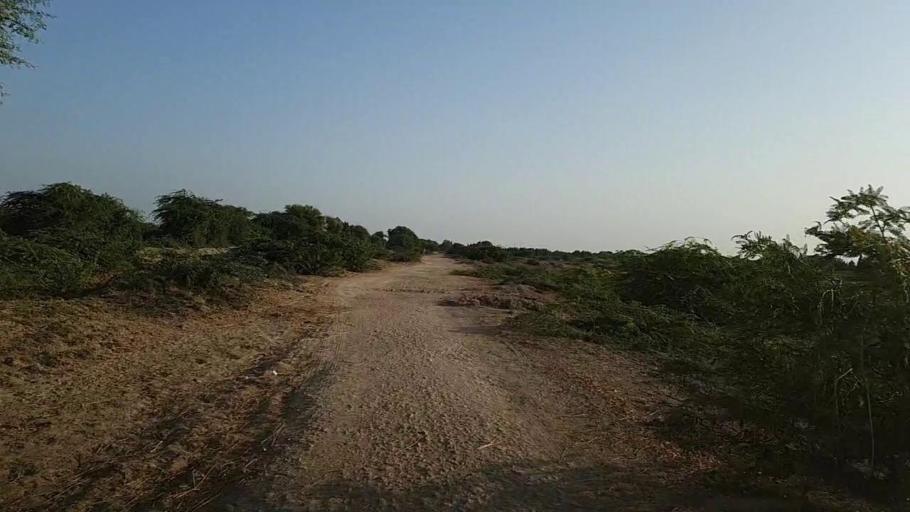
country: PK
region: Sindh
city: Kario
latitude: 24.7168
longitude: 68.6673
